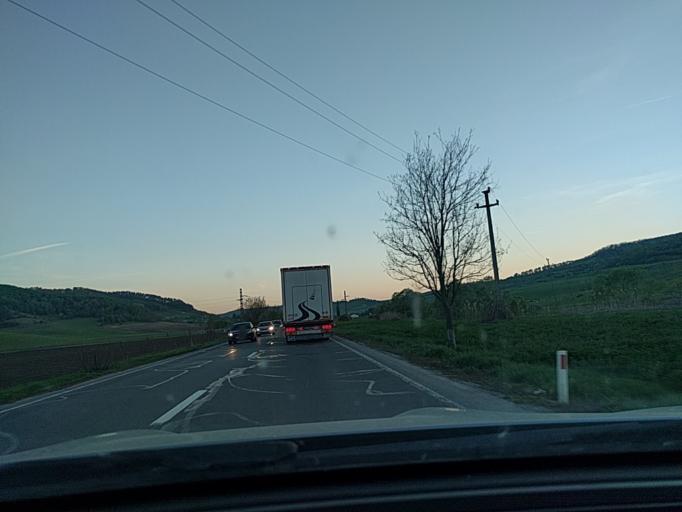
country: RO
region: Mures
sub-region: Comuna Balauseri
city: Chendu
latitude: 46.3671
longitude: 24.7232
